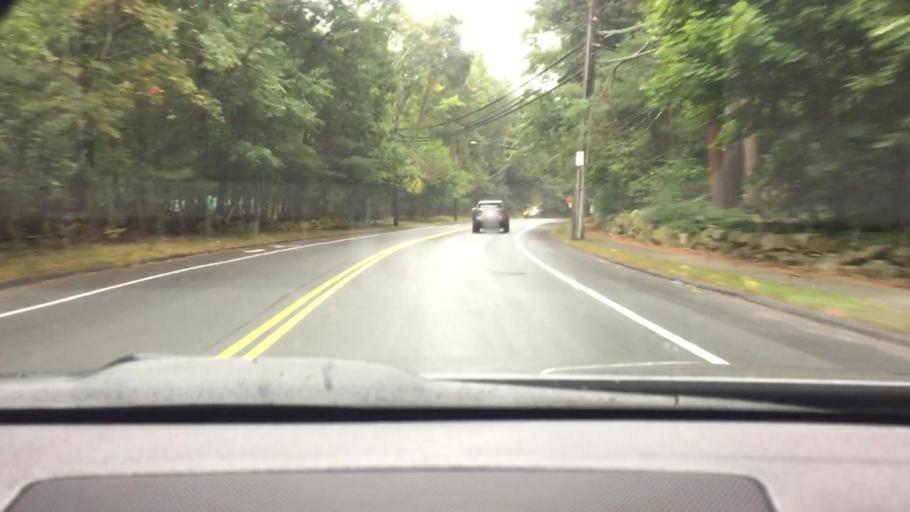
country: US
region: Massachusetts
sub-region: Norfolk County
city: Needham
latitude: 42.3000
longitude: -71.2031
